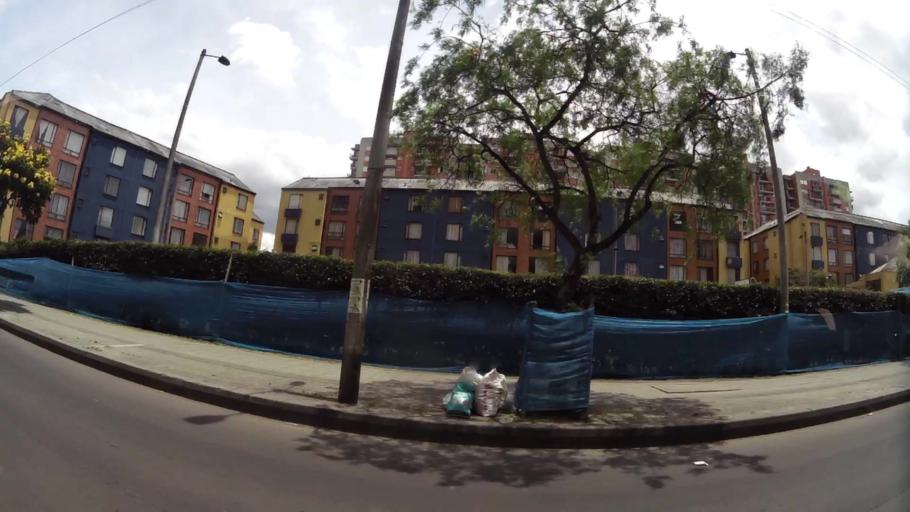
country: CO
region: Bogota D.C.
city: Bogota
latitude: 4.6430
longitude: -74.1451
